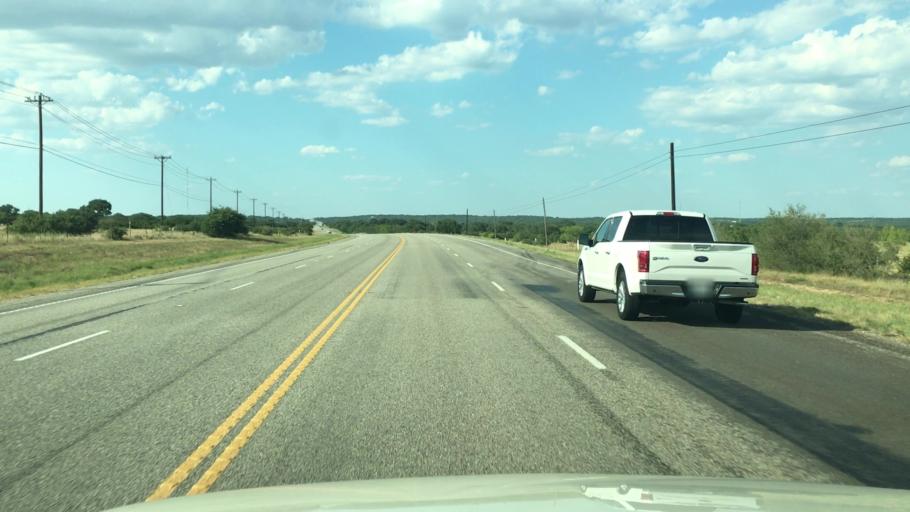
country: US
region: Texas
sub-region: Llano County
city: Horseshoe Bay
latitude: 30.4101
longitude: -98.3533
